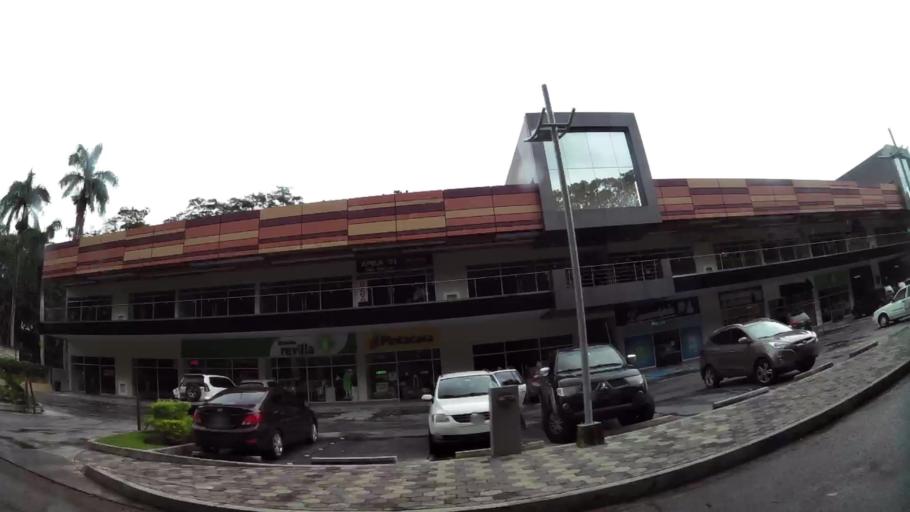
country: PA
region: Panama
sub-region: Distrito de Panama
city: Ancon
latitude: 9.0038
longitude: -79.5733
